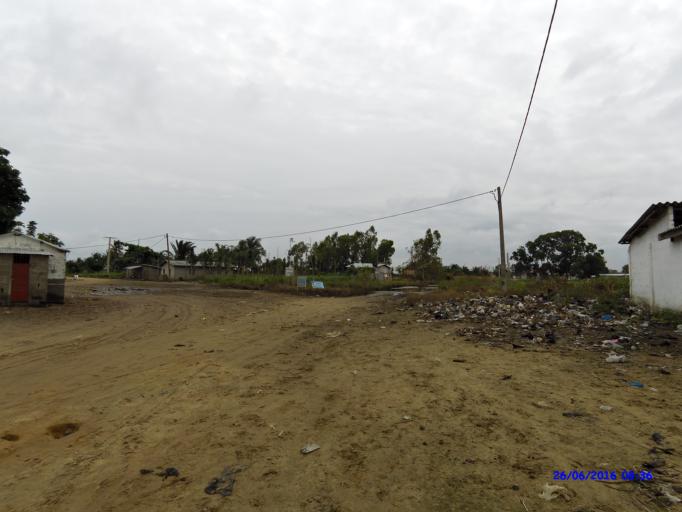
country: BJ
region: Atlantique
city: Hevie
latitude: 6.3550
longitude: 2.3071
